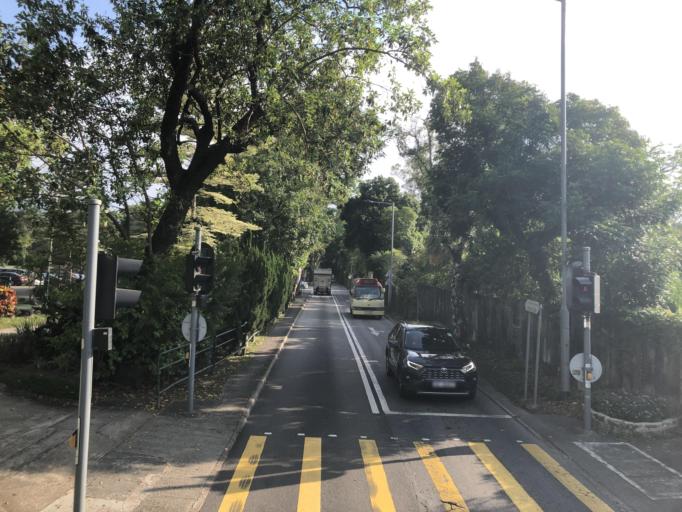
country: HK
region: Tai Po
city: Tai Po
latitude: 22.4962
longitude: 114.1217
